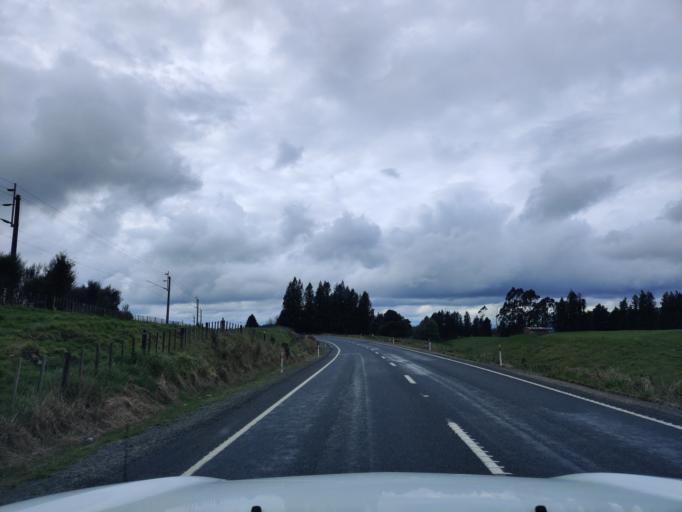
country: NZ
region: Waikato
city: Turangi
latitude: -39.0292
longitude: 175.3822
